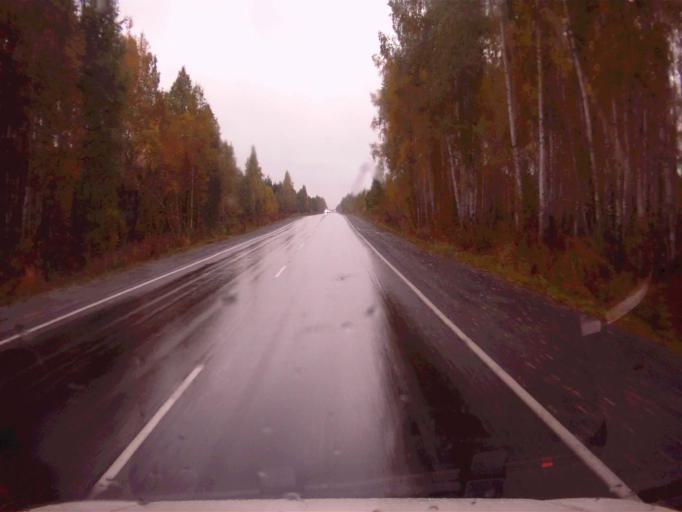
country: RU
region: Chelyabinsk
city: Tayginka
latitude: 55.5364
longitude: 60.6467
